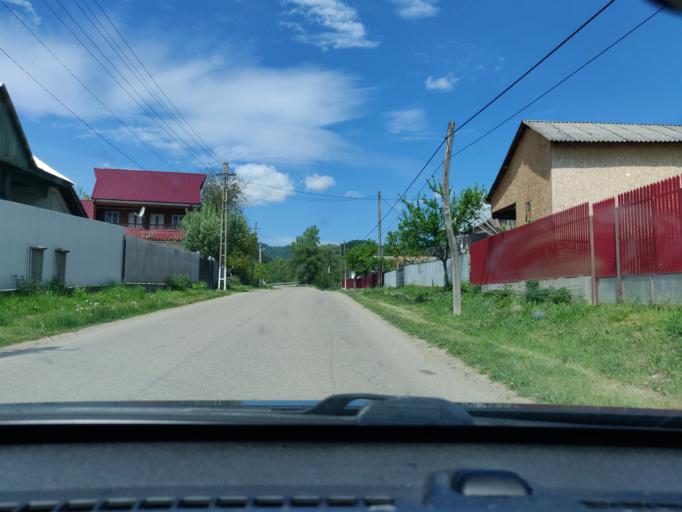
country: RO
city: Vizantea-Manastireasca
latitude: 45.9825
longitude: 26.7871
